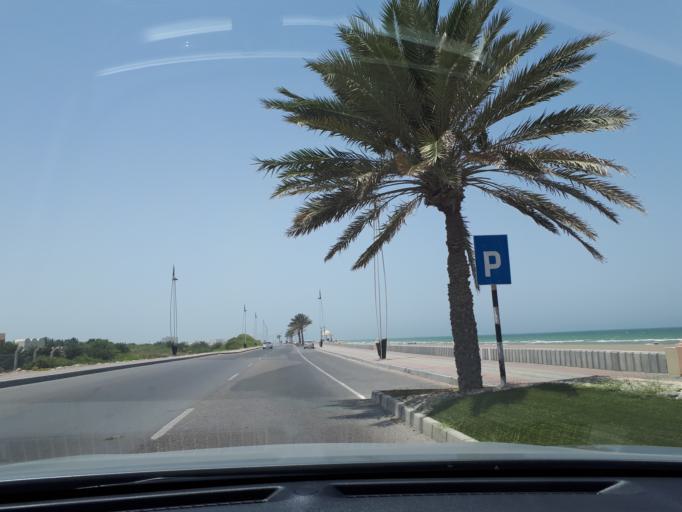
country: OM
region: Muhafazat Masqat
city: As Sib al Jadidah
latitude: 23.6484
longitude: 58.2353
